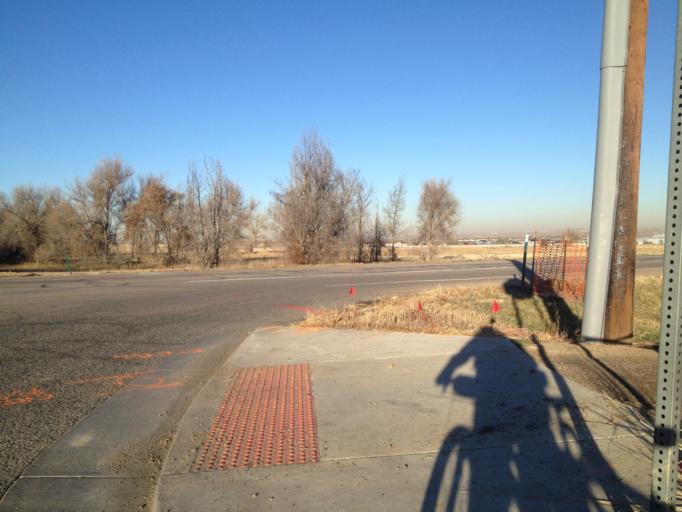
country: US
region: Colorado
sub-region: Boulder County
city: Louisville
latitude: 39.9722
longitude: -105.1093
